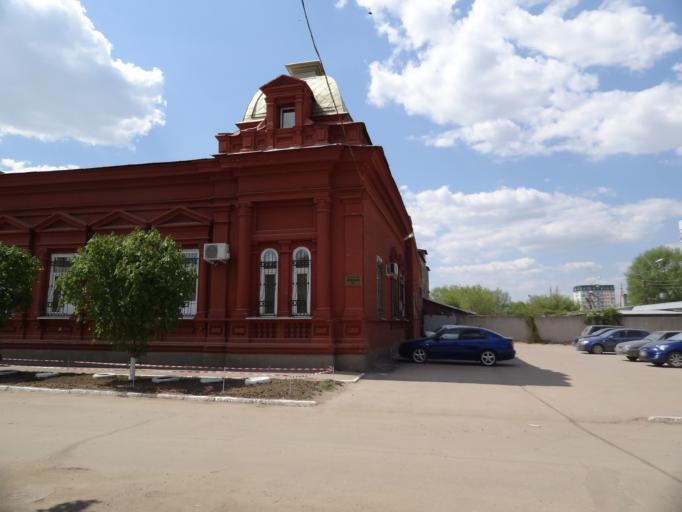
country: RU
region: Saratov
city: Engel's
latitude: 51.5006
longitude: 46.1320
